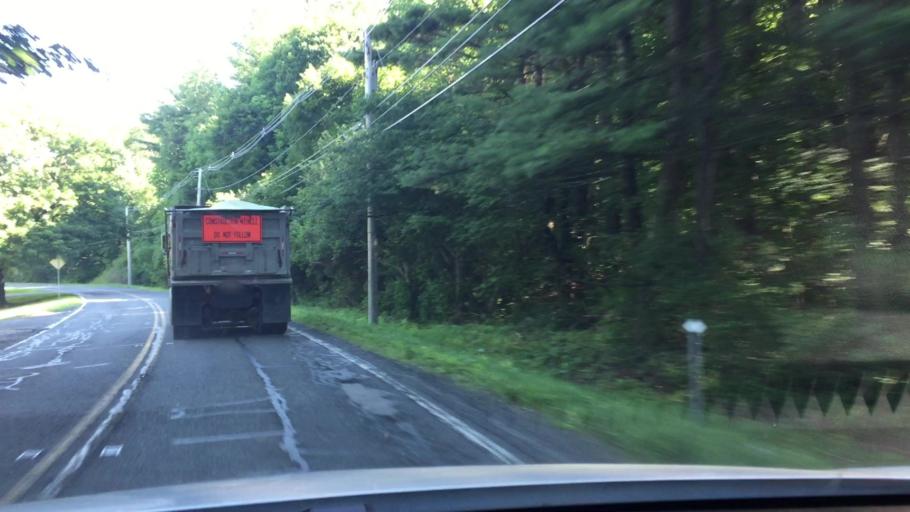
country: US
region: Massachusetts
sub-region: Berkshire County
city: West Stockbridge
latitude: 42.3208
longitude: -73.3676
